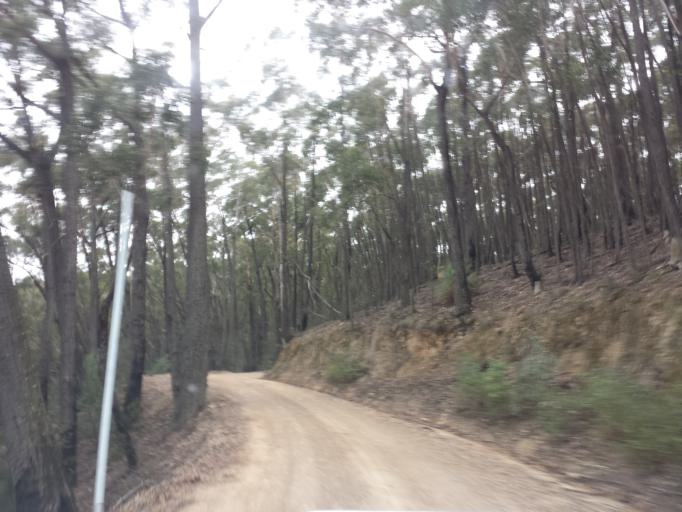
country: AU
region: Victoria
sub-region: Latrobe
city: Traralgon
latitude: -37.9775
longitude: 146.4360
